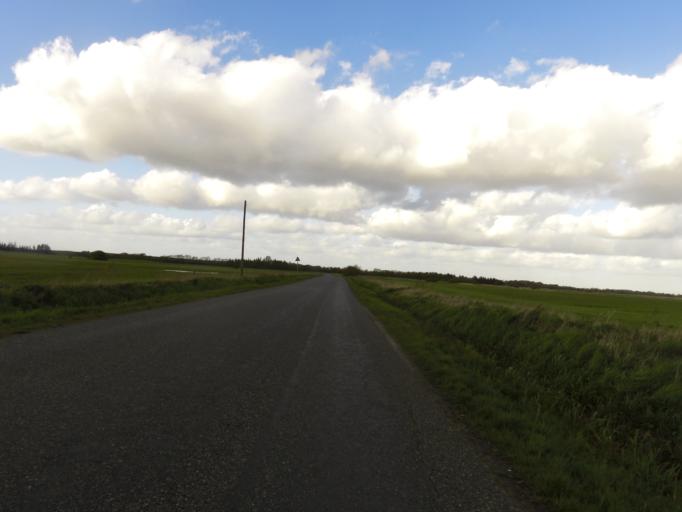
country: DK
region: South Denmark
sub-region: Esbjerg Kommune
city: Ribe
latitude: 55.3269
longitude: 8.8115
